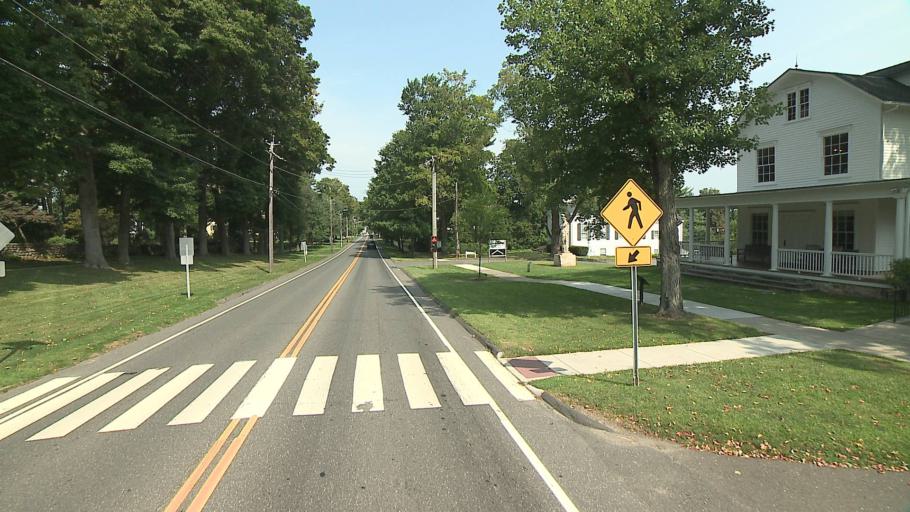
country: US
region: Connecticut
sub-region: Fairfield County
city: Ridgefield
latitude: 41.2766
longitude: -73.4977
